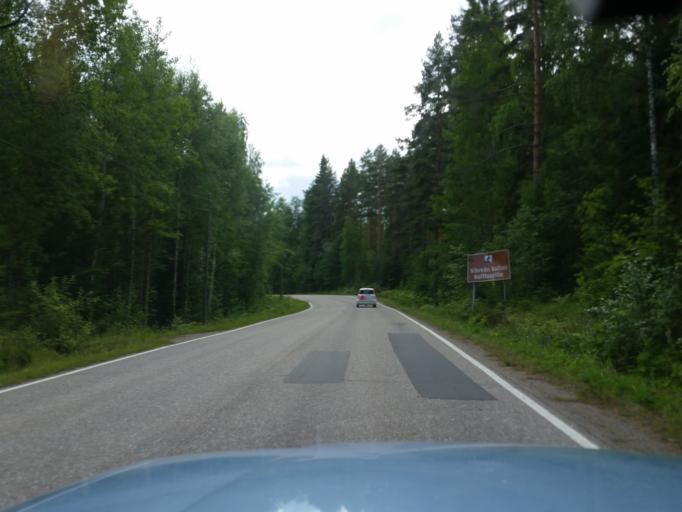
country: FI
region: Southern Savonia
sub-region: Savonlinna
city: Sulkava
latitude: 61.7762
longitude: 28.3618
